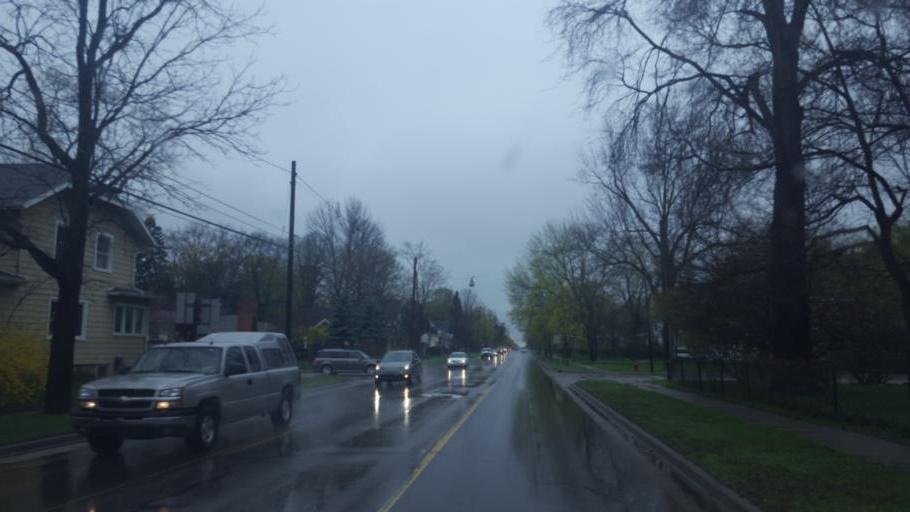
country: US
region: Michigan
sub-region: Isabella County
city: Mount Pleasant
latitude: 43.5972
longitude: -84.7713
